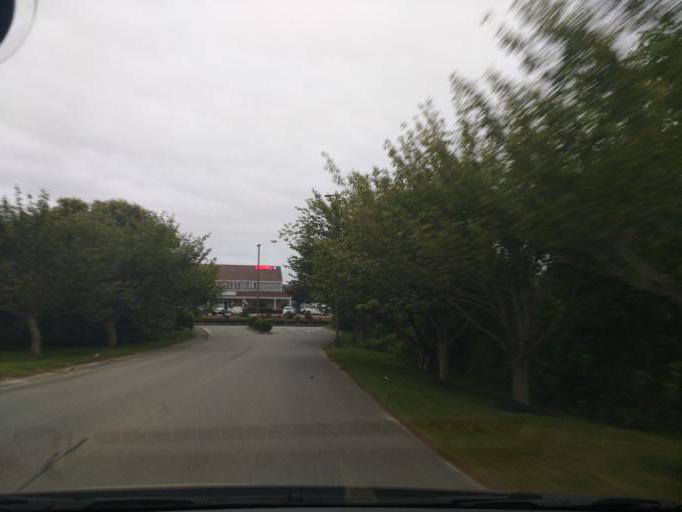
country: US
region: Massachusetts
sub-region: Barnstable County
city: Teaticket
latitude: 41.5600
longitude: -70.5942
